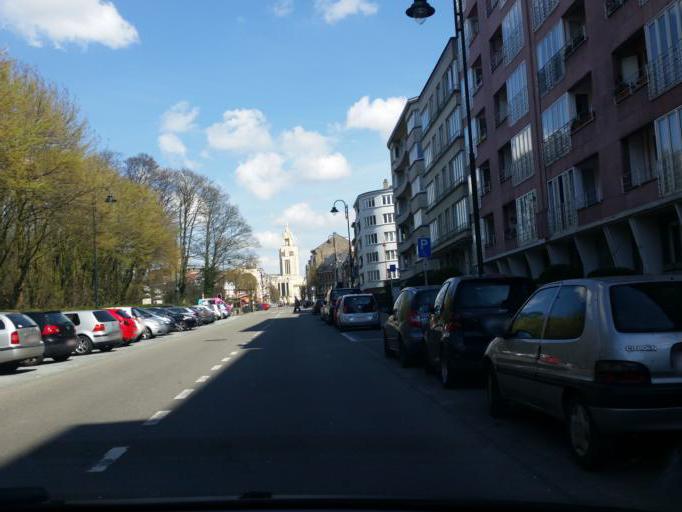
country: BE
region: Flanders
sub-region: Provincie Vlaams-Brabant
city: Drogenbos
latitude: 50.8141
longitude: 4.3315
